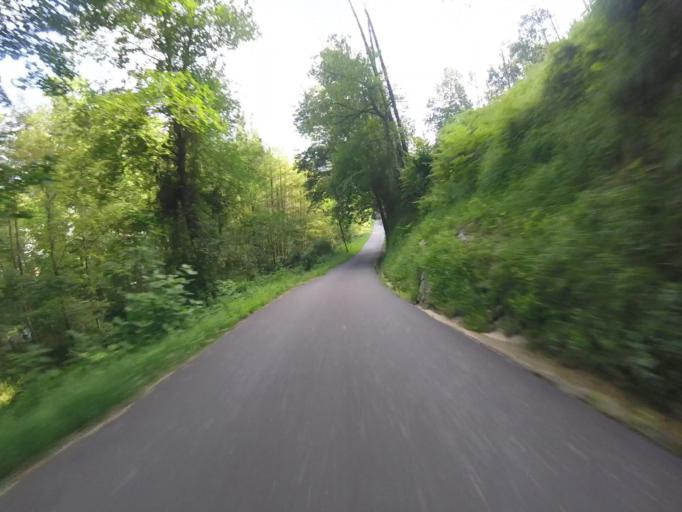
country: ES
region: Basque Country
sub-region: Provincia de Guipuzcoa
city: Astigarraga
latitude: 43.2549
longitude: -1.9500
